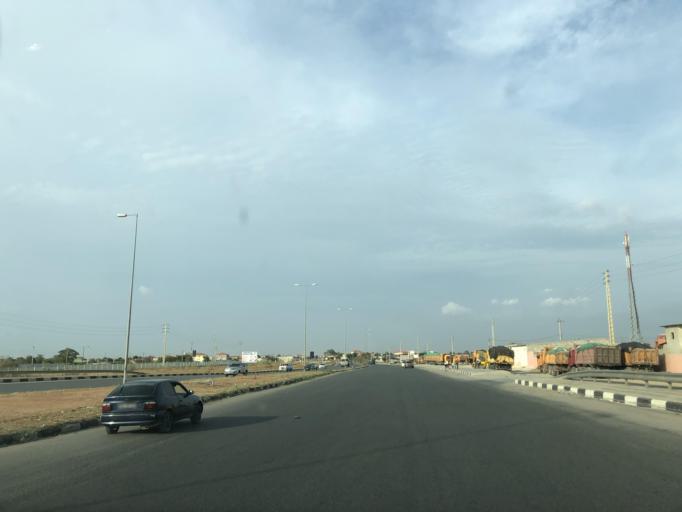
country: AO
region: Luanda
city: Luanda
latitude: -8.9338
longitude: 13.2999
